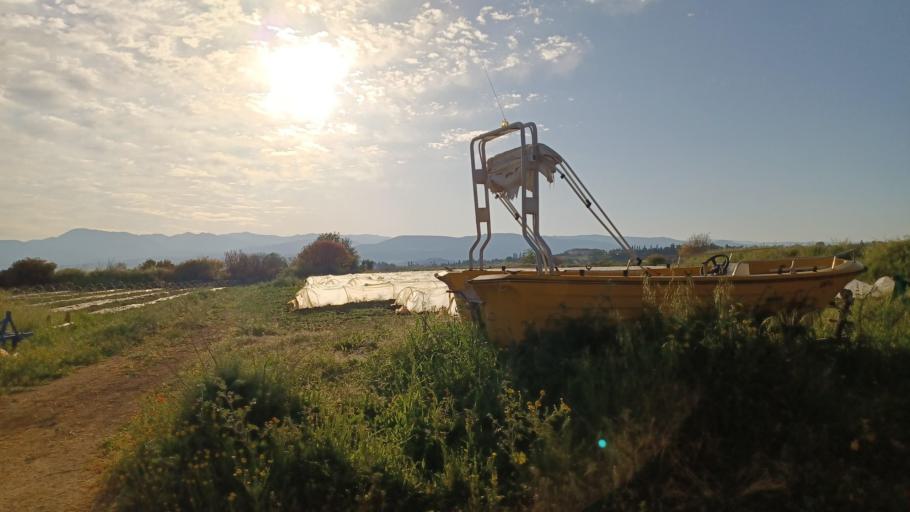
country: CY
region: Pafos
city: Polis
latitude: 35.0296
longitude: 32.3987
